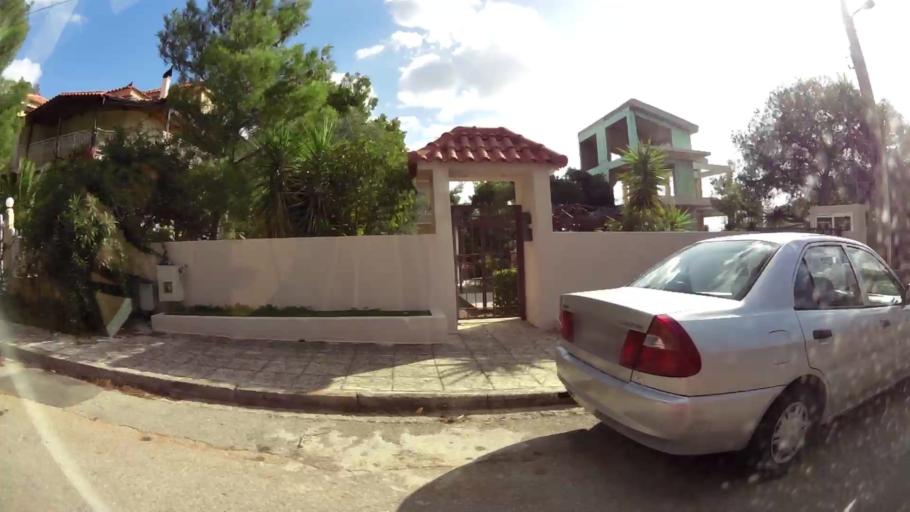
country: GR
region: Attica
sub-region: Nomarchia Anatolikis Attikis
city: Thrakomakedones
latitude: 38.1301
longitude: 23.7673
